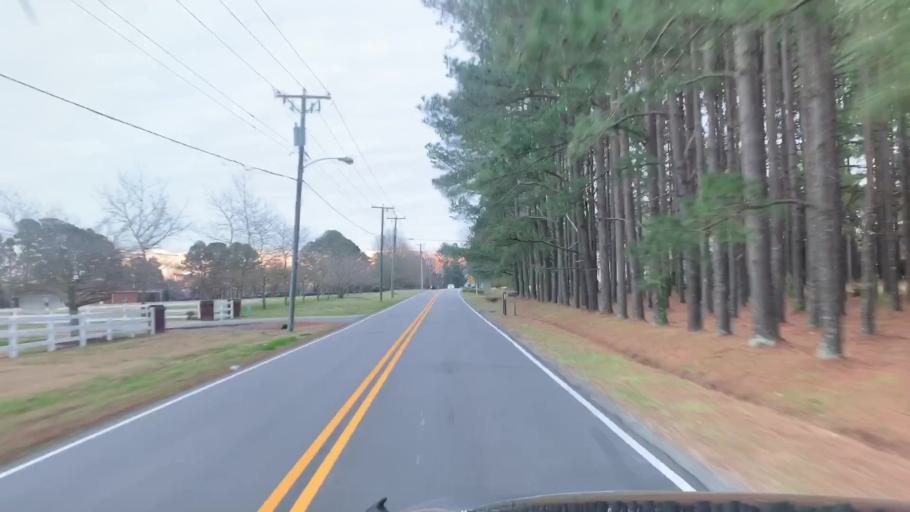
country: US
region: North Carolina
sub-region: Currituck County
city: Moyock
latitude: 36.6420
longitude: -76.2074
